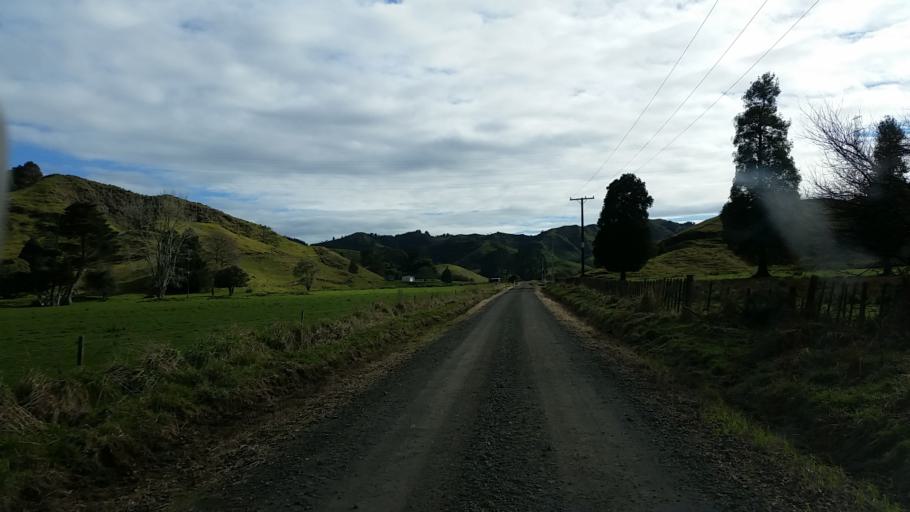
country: NZ
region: Taranaki
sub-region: South Taranaki District
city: Eltham
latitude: -39.2340
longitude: 174.5685
